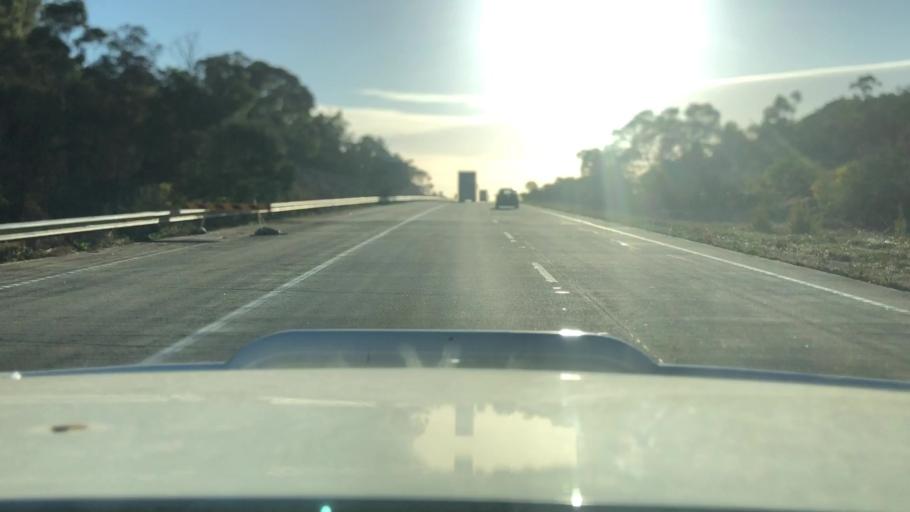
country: AU
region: New South Wales
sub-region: Wingecarribee
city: Bowral
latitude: -34.4564
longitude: 150.3617
